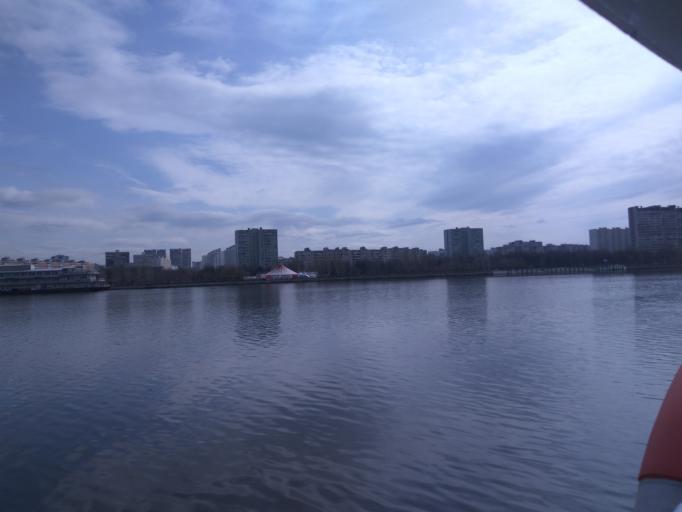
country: RU
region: Moscow
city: Kolomenskoye
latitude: 55.6858
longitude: 37.7101
